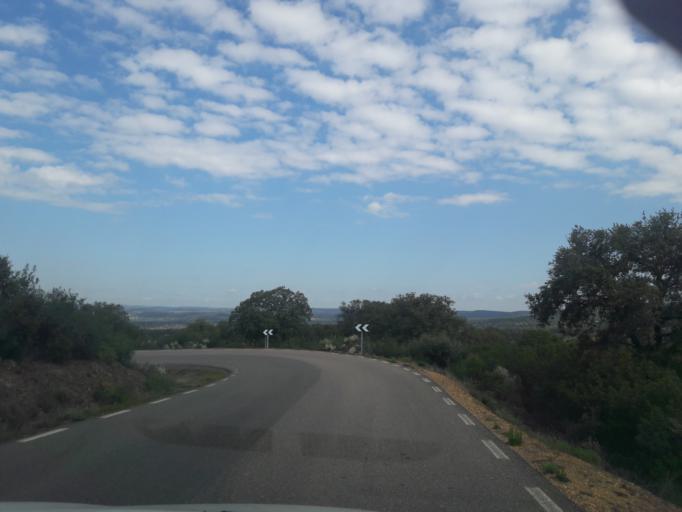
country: ES
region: Castille and Leon
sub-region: Provincia de Salamanca
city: Zamarra
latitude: 40.5481
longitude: -6.4265
